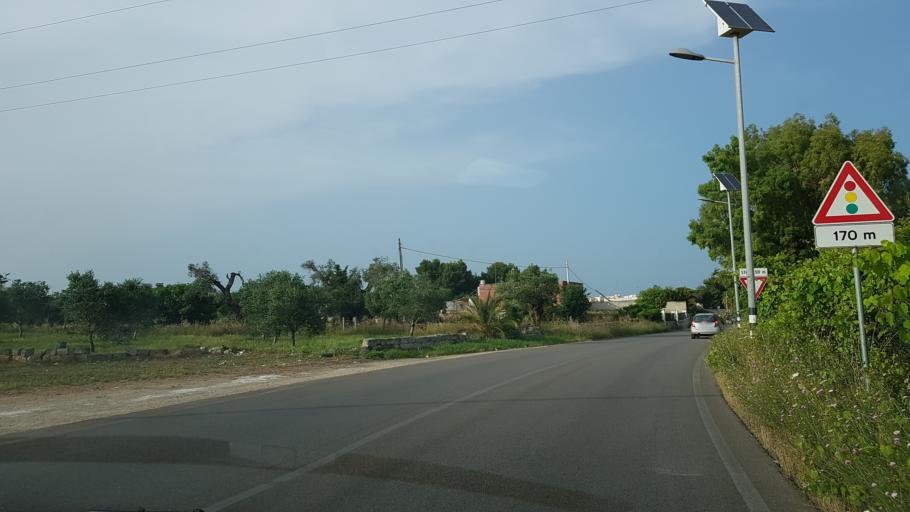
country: IT
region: Apulia
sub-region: Provincia di Brindisi
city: San Pietro Vernotico
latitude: 40.4836
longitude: 17.9870
